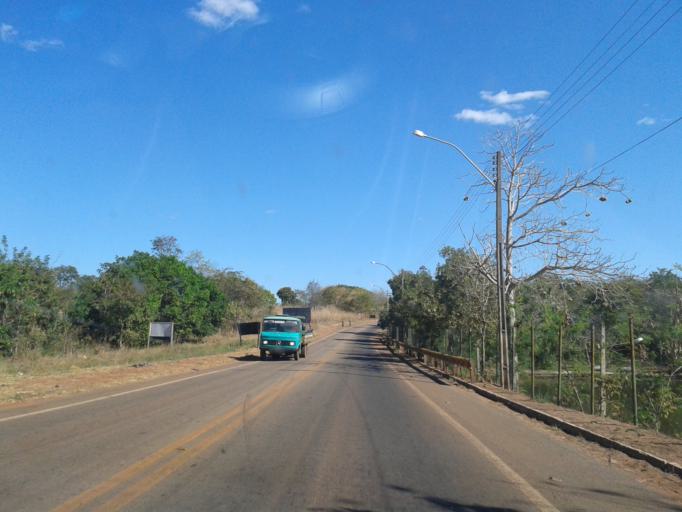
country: BR
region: Goias
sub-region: Crixas
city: Crixas
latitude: -14.1050
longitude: -50.3398
